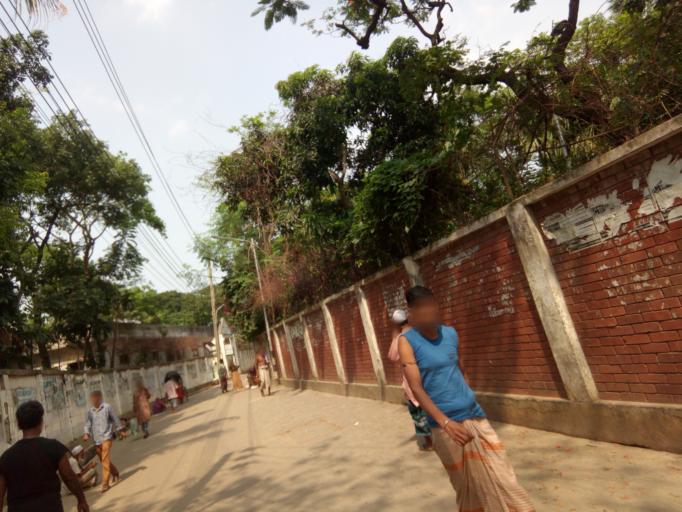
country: BD
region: Dhaka
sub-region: Dhaka
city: Dhaka
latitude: 23.6962
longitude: 90.4281
